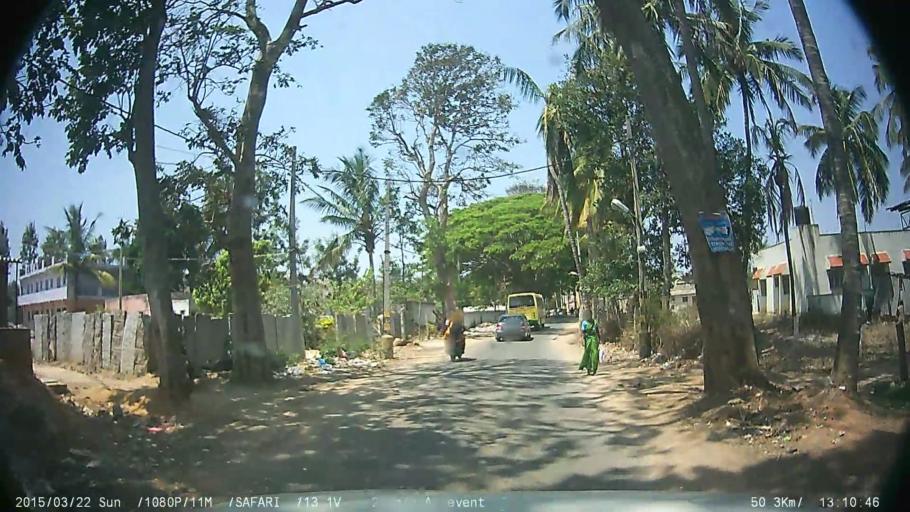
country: IN
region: Karnataka
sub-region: Bangalore Urban
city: Anekal
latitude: 12.8056
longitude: 77.5788
